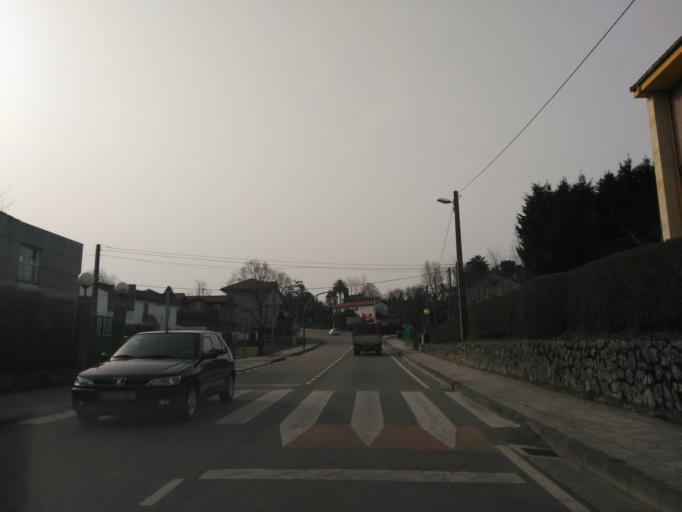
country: ES
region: Cantabria
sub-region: Provincia de Cantabria
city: Comillas
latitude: 43.3807
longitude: -4.2897
